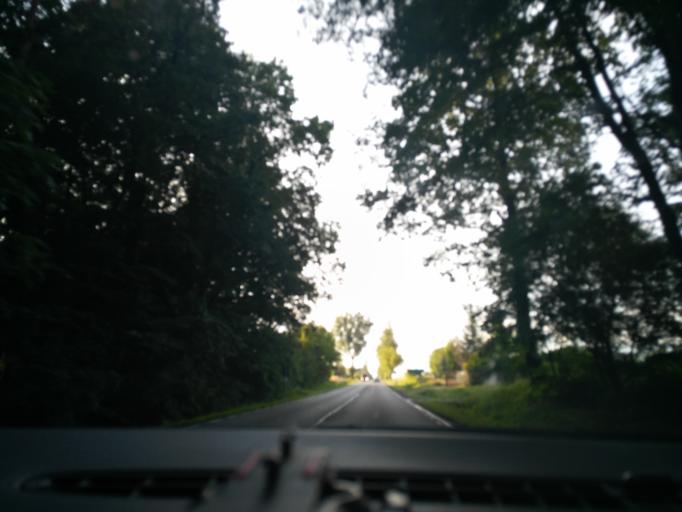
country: PL
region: Lublin Voivodeship
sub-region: Powiat krasnicki
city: Szastarka
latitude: 50.8643
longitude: 22.2767
